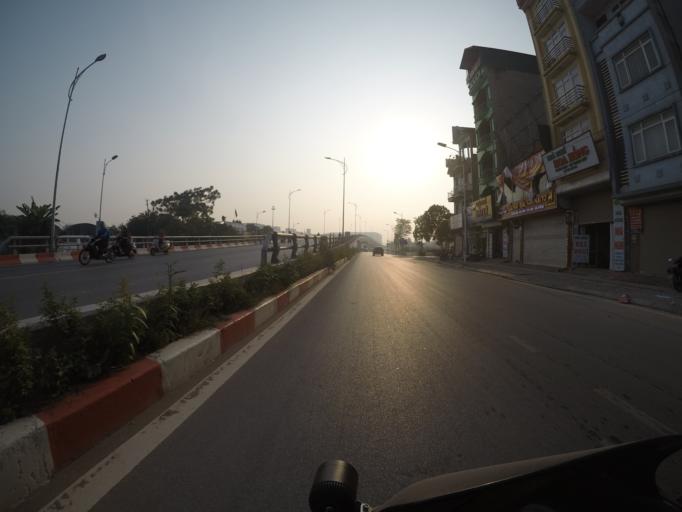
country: VN
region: Ha Noi
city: Trau Quy
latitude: 21.0276
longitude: 105.8946
